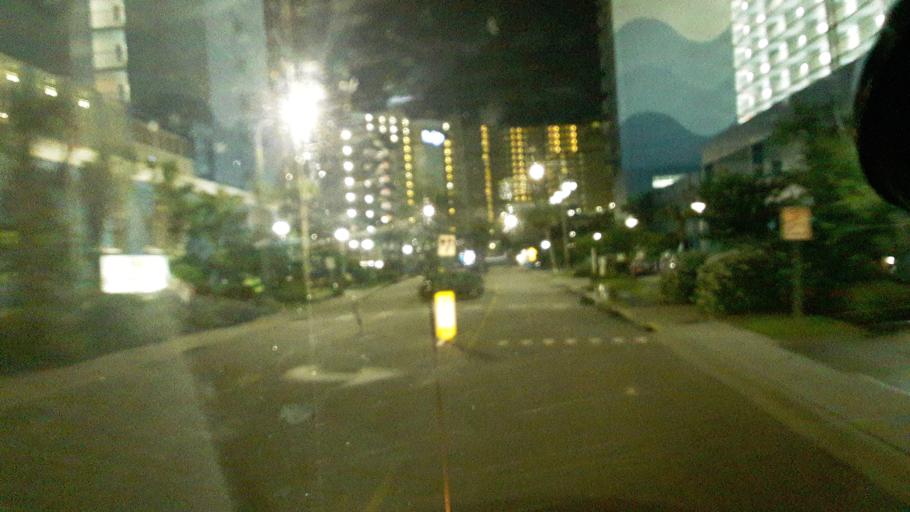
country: US
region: South Carolina
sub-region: Horry County
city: North Myrtle Beach
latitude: 33.7921
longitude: -78.7328
